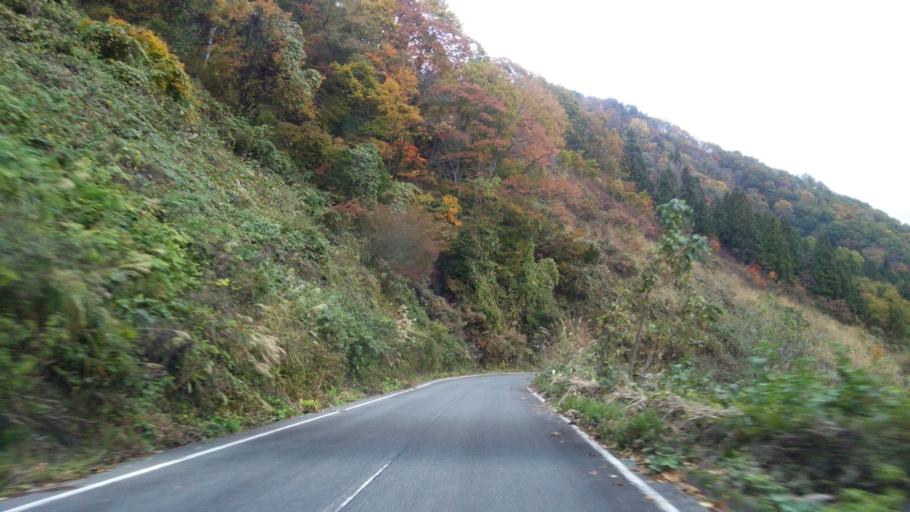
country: JP
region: Fukushima
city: Kitakata
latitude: 37.4178
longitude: 139.7695
